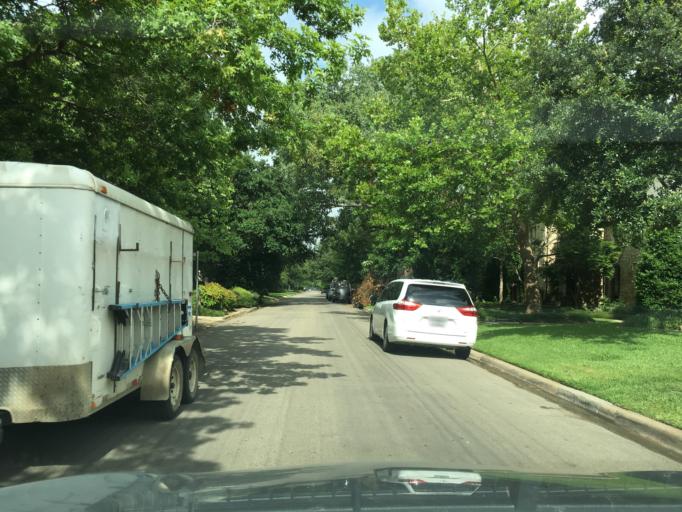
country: US
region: Texas
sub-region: Dallas County
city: University Park
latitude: 32.8823
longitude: -96.7969
